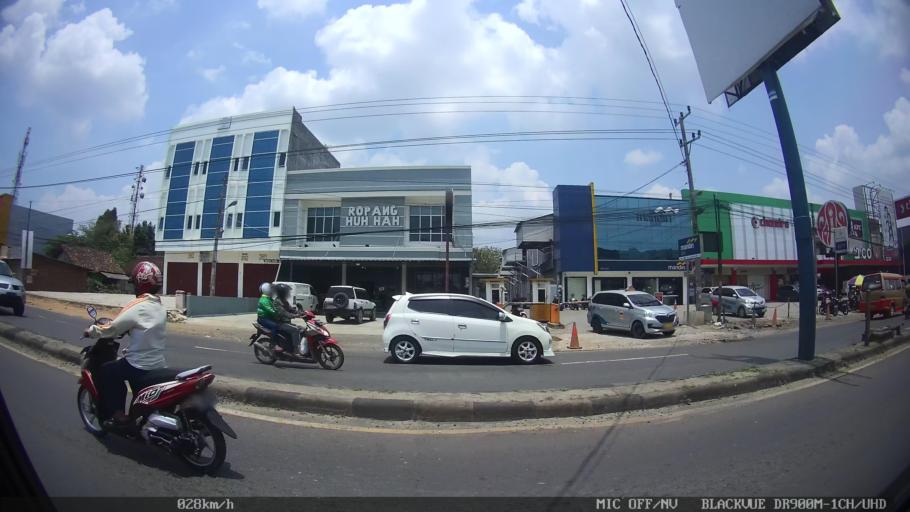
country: ID
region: Lampung
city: Natar
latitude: -5.3098
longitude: 105.1939
